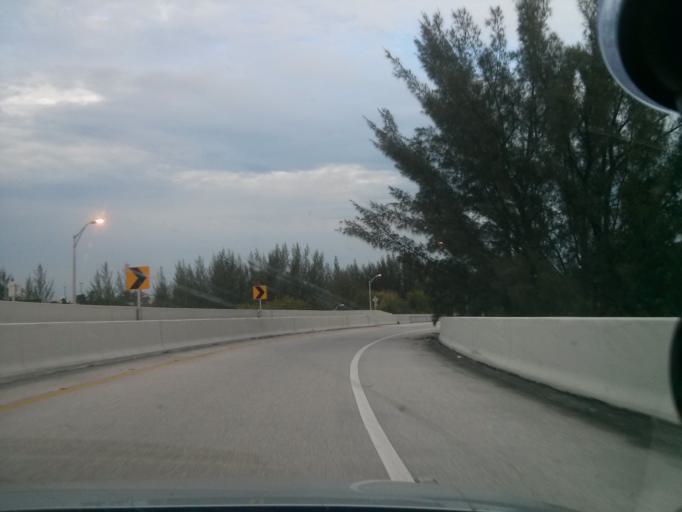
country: US
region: Florida
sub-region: Miami-Dade County
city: Virginia Gardens
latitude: 25.7967
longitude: -80.3082
